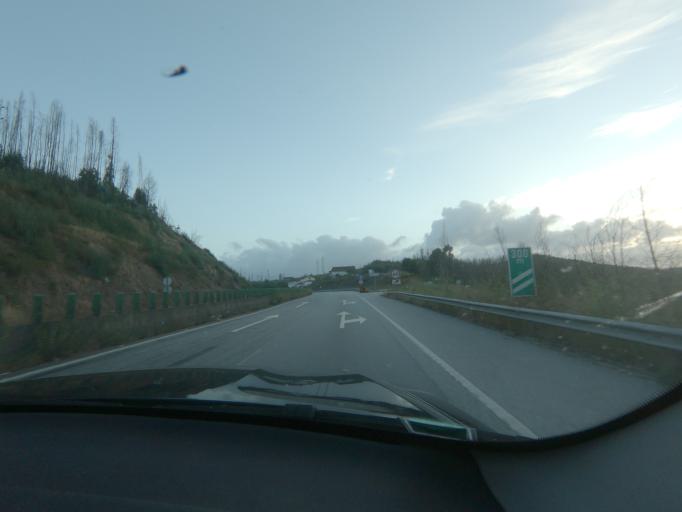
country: PT
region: Coimbra
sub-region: Penacova
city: Penacova
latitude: 40.3120
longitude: -8.2330
